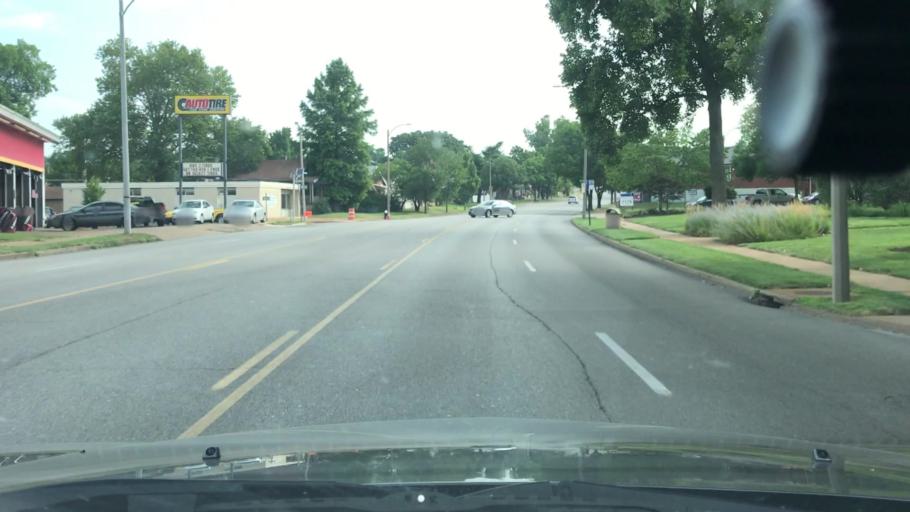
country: US
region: Missouri
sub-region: Saint Louis County
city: Maplewood
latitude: 38.6040
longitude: -90.2913
